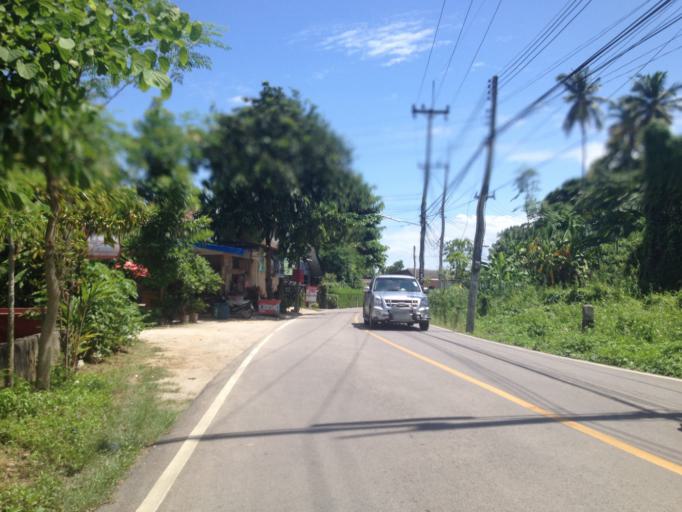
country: TH
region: Chiang Mai
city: Hang Dong
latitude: 18.6862
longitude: 98.9264
